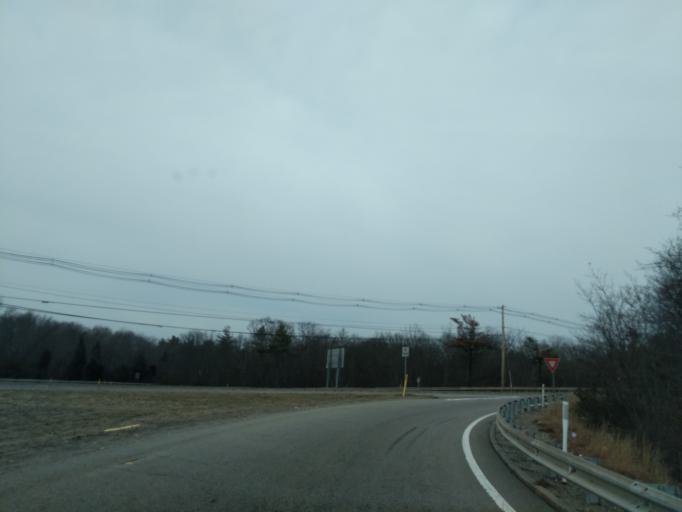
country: US
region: Massachusetts
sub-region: Bristol County
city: Raynham Center
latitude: 41.9061
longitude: -71.0443
